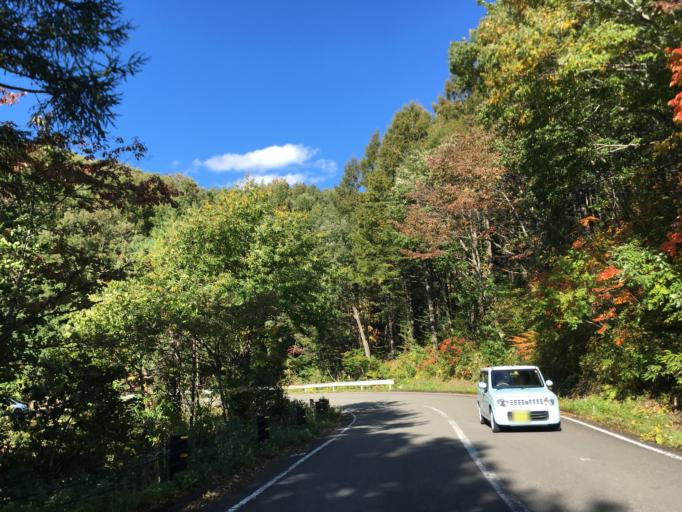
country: JP
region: Fukushima
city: Inawashiro
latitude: 37.6539
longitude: 140.1628
